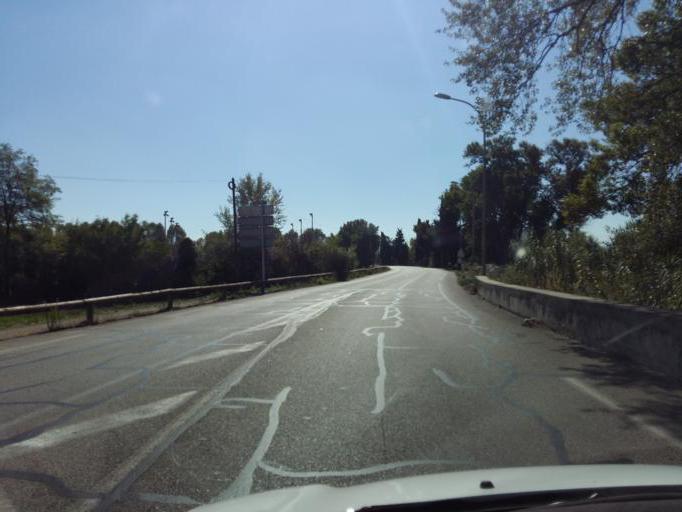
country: FR
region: Provence-Alpes-Cote d'Azur
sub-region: Departement du Vaucluse
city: Cavaillon
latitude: 43.8236
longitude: 5.0365
